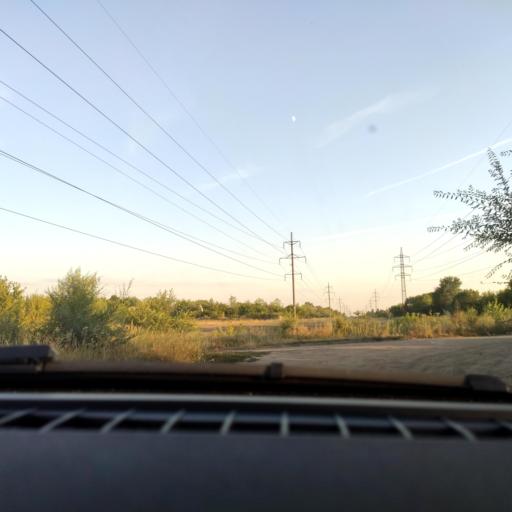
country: RU
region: Voronezj
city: Maslovka
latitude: 51.6142
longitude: 39.2725
